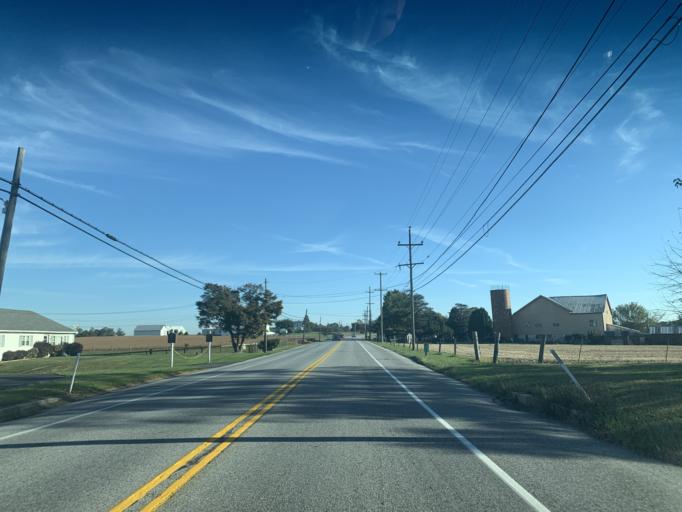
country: US
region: Pennsylvania
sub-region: Chester County
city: Oxford
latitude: 39.8347
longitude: -75.9492
